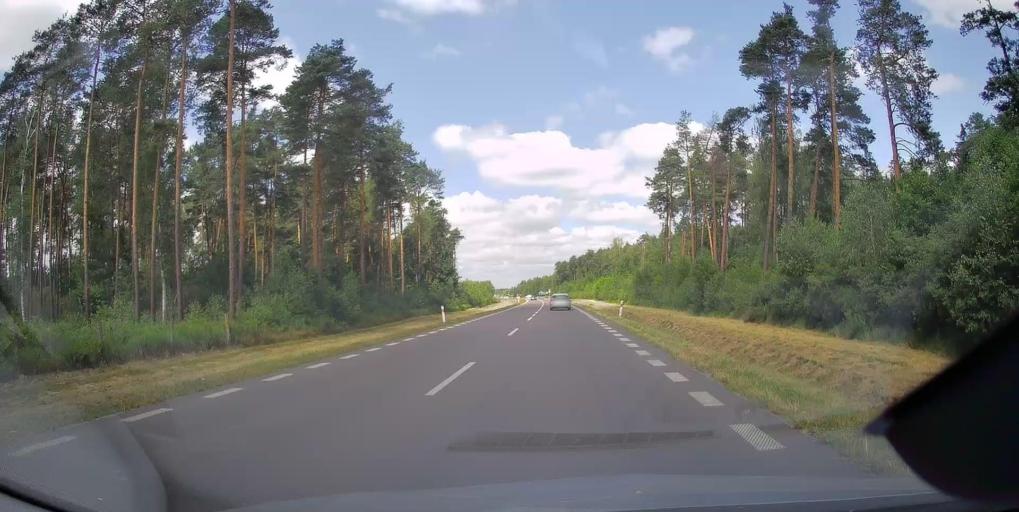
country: PL
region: Subcarpathian Voivodeship
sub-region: Powiat mielecki
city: Mielec
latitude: 50.3214
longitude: 21.4962
